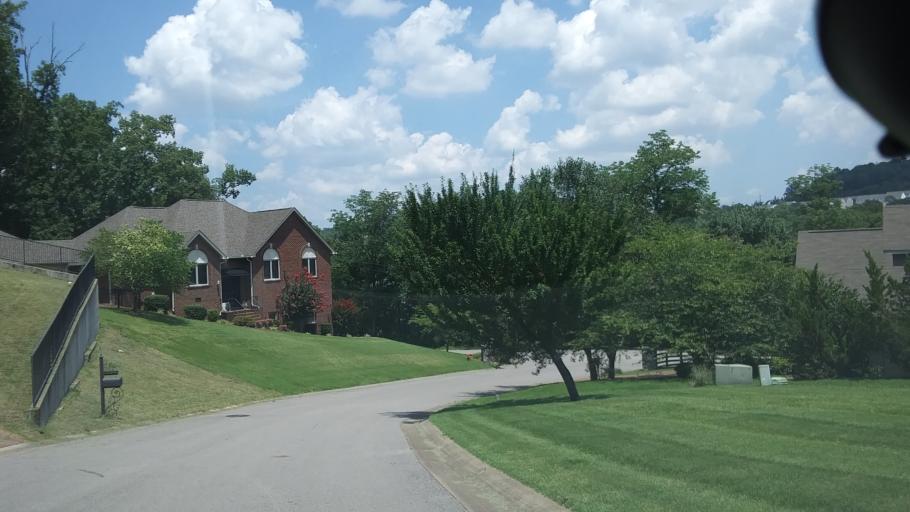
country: US
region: Tennessee
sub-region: Davidson County
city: Belle Meade
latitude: 36.1178
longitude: -86.9266
